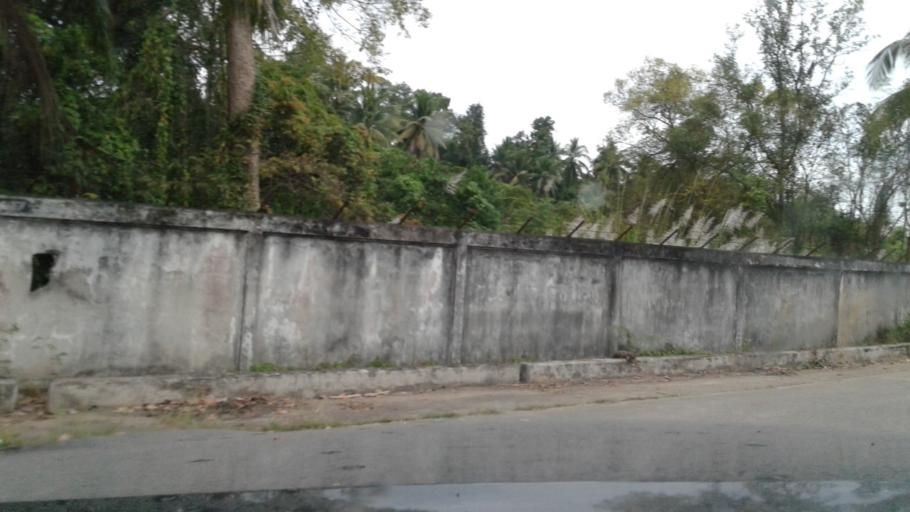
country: TH
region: Changwat Udon Thani
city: Nong Wua So
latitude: 17.2296
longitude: 102.5341
